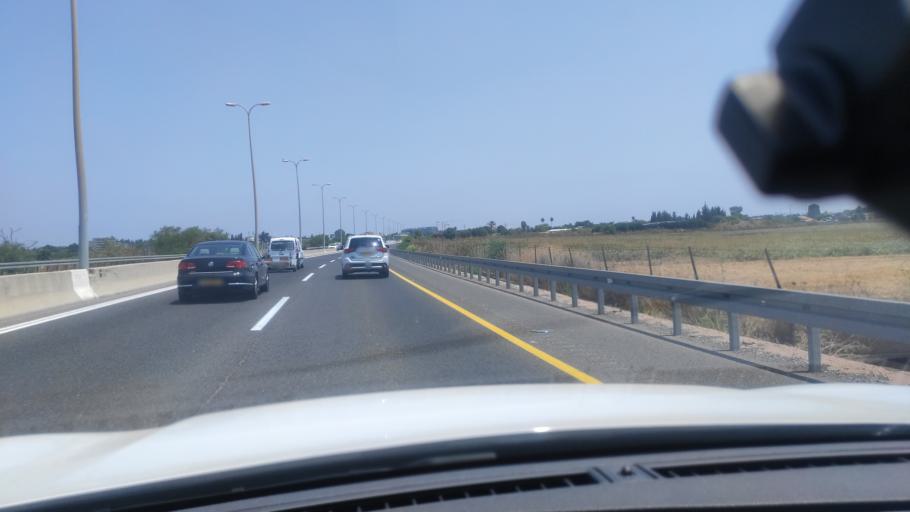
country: IL
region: Central District
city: Hod HaSharon
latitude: 32.1459
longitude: 34.9184
